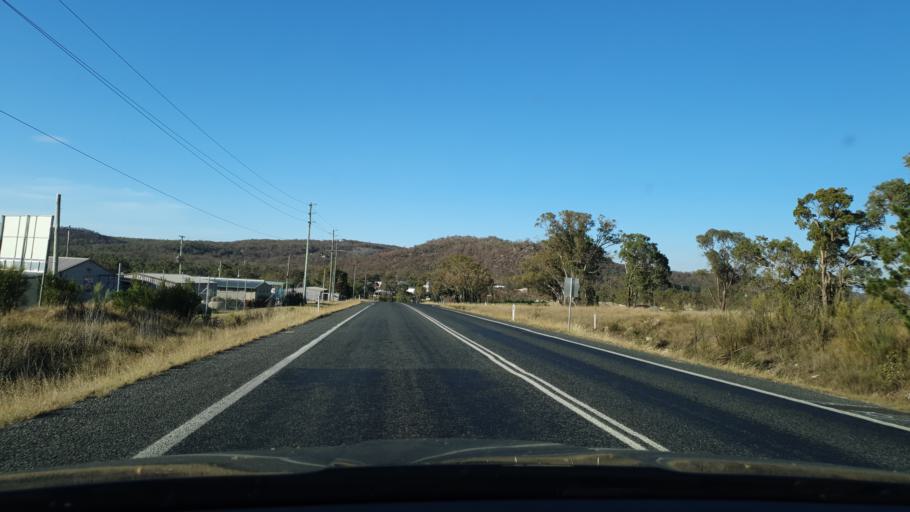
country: AU
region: Queensland
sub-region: Southern Downs
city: Stanthorpe
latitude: -28.6578
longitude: 151.9170
